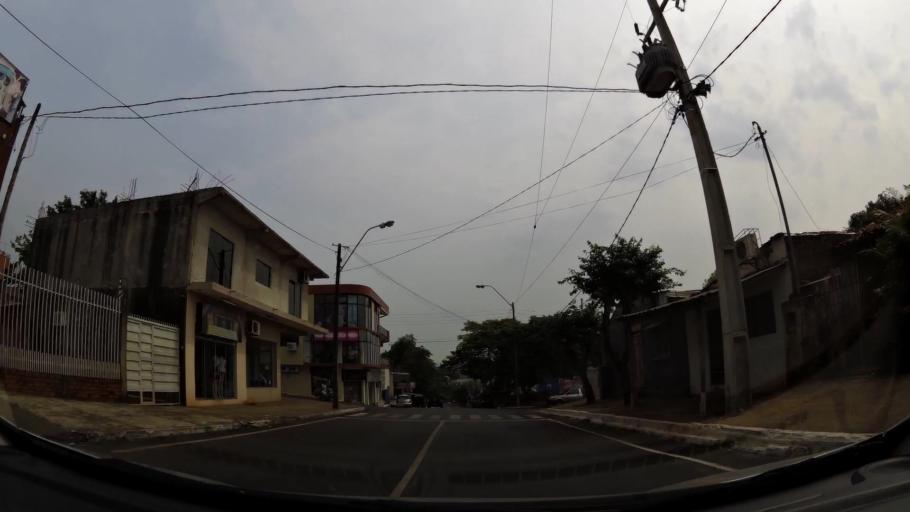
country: BR
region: Parana
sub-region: Foz Do Iguacu
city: Foz do Iguacu
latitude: -25.5511
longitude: -54.6068
